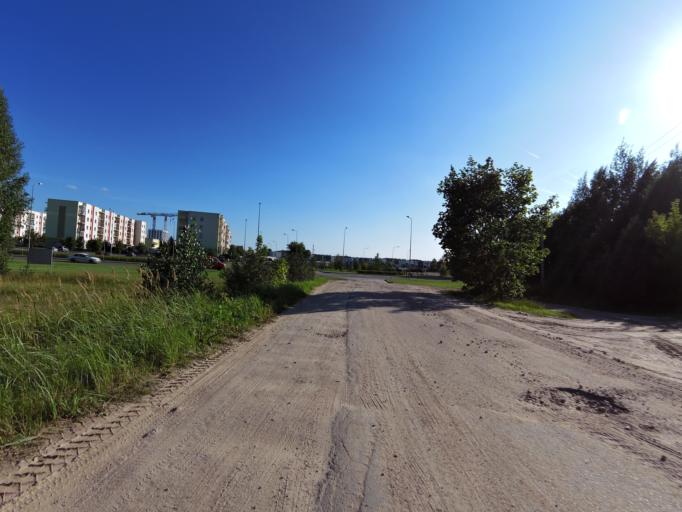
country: LT
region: Vilnius County
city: Pilaite
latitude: 54.7111
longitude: 25.1728
